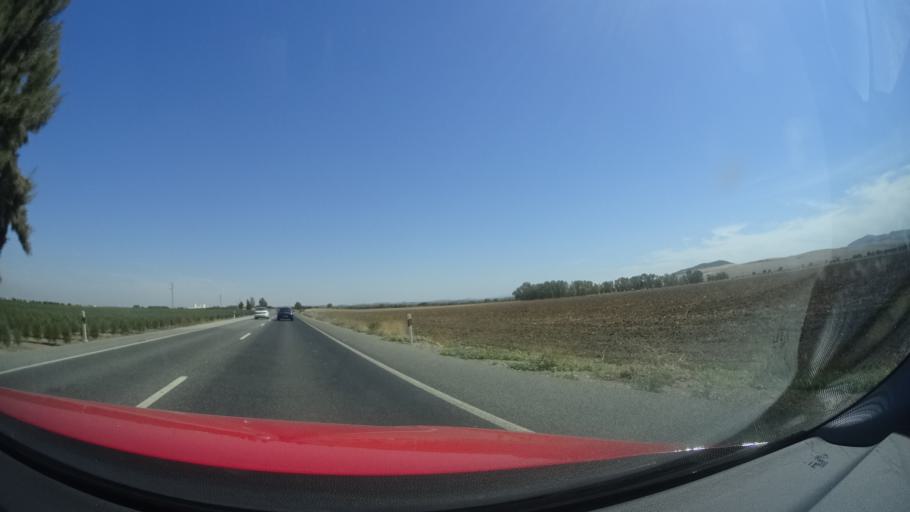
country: ES
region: Andalusia
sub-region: Provincia de Sevilla
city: Las Cabezas de San Juan
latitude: 36.9039
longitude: -5.9810
